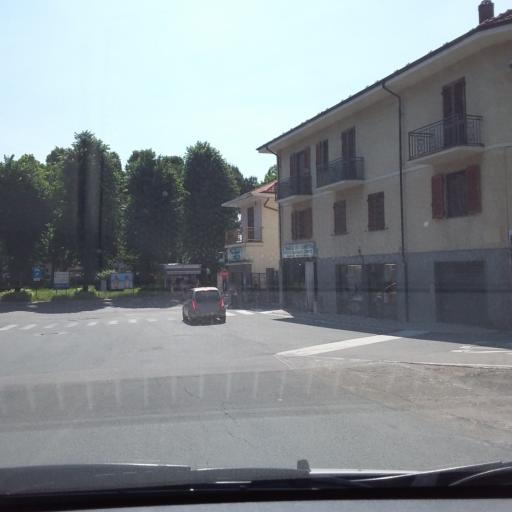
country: IT
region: Piedmont
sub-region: Provincia di Torino
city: Rivoli
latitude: 45.0630
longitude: 7.5178
